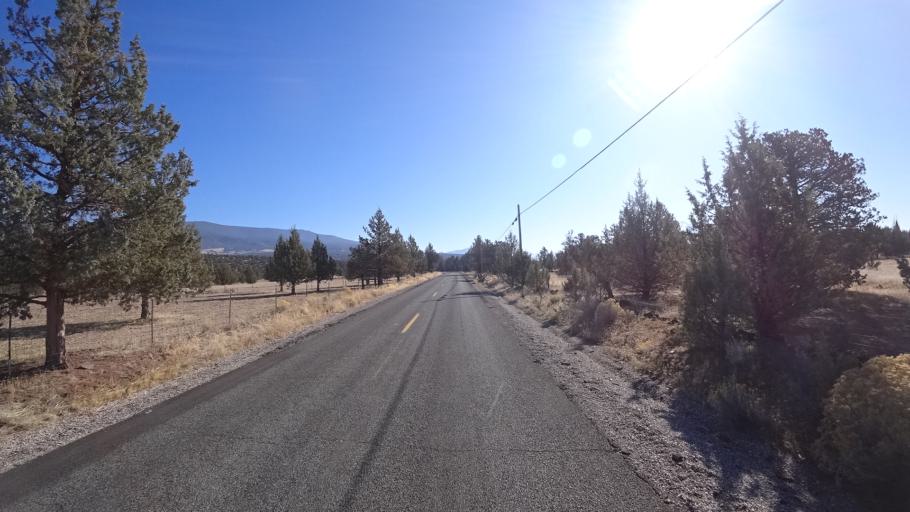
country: US
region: California
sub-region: Siskiyou County
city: Montague
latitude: 41.6422
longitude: -122.3479
